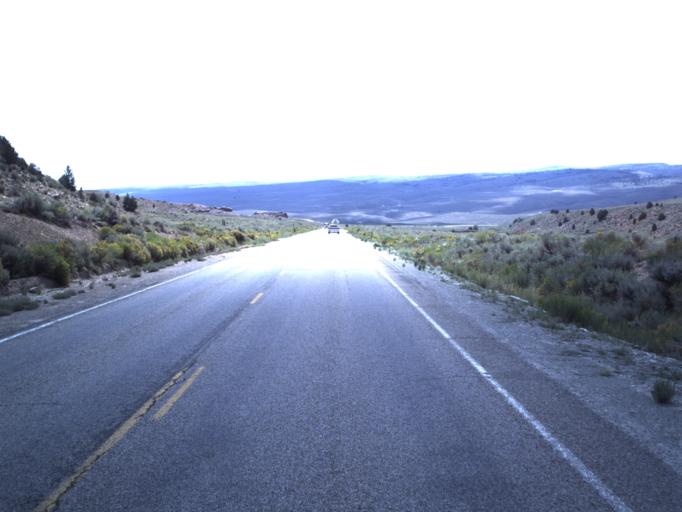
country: US
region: Utah
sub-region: Carbon County
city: Helper
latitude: 39.8251
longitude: -110.7868
